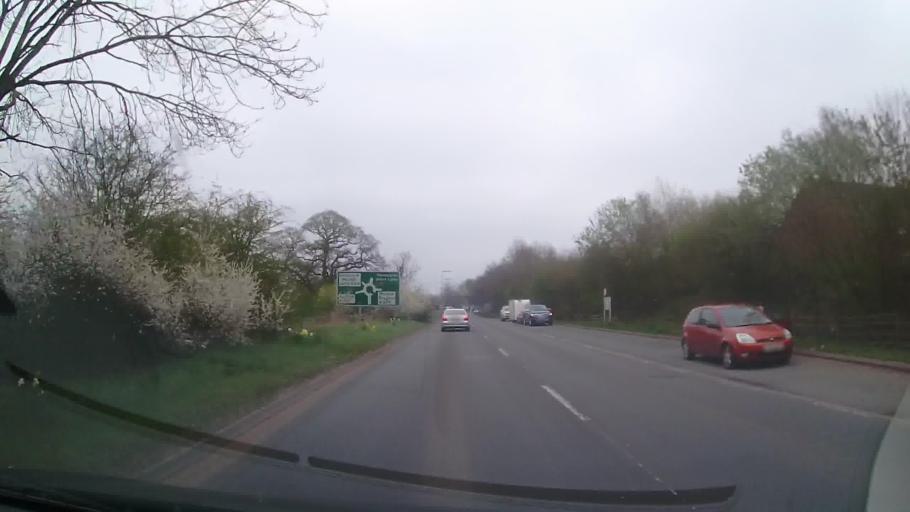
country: GB
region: England
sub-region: Shropshire
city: Market Drayton
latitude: 52.9118
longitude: -2.4927
